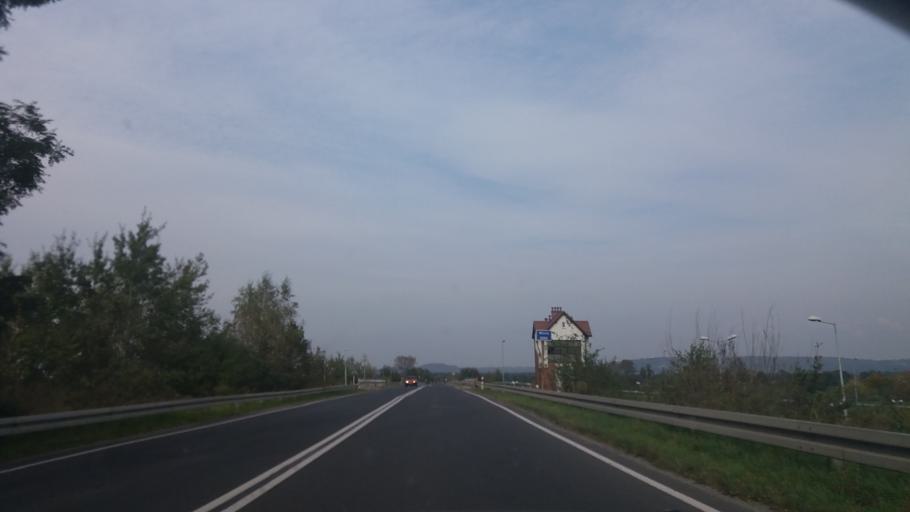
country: PL
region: Lesser Poland Voivodeship
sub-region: Powiat oswiecimski
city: Zator
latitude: 50.0286
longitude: 19.4367
